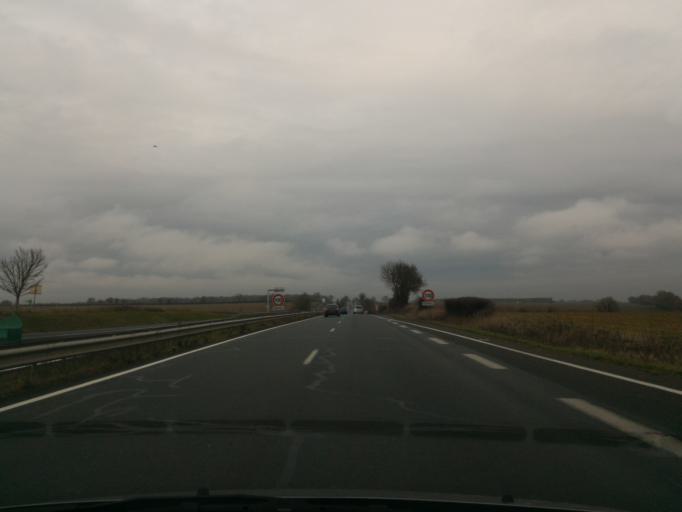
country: FR
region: Poitou-Charentes
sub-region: Departement de la Vienne
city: Vivonne
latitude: 46.4385
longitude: 0.2648
